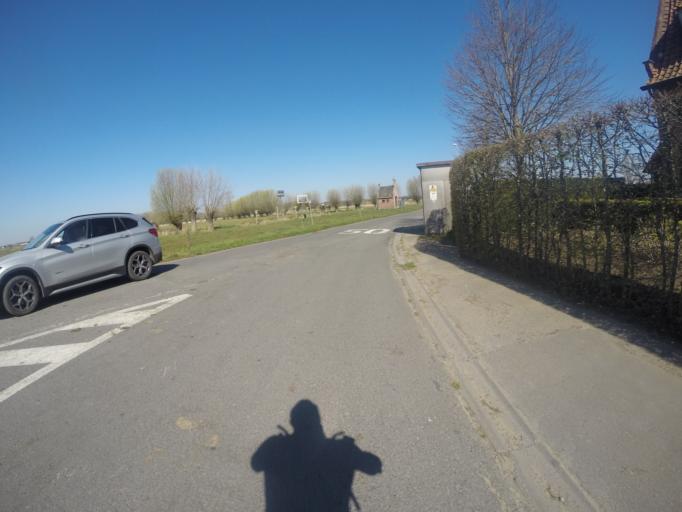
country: BE
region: Flanders
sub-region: Provincie West-Vlaanderen
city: Ruiselede
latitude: 51.0644
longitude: 3.3871
